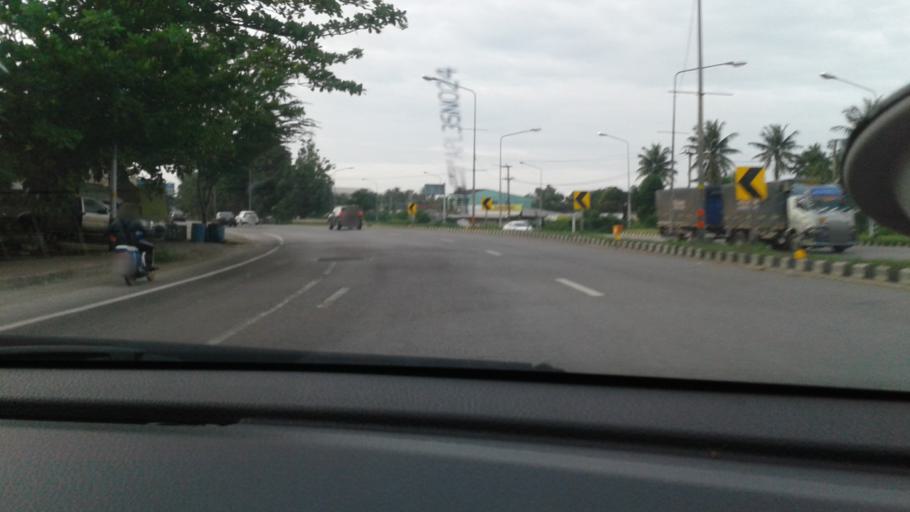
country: TH
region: Prachuap Khiri Khan
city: Pran Buri
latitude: 12.4199
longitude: 99.9246
